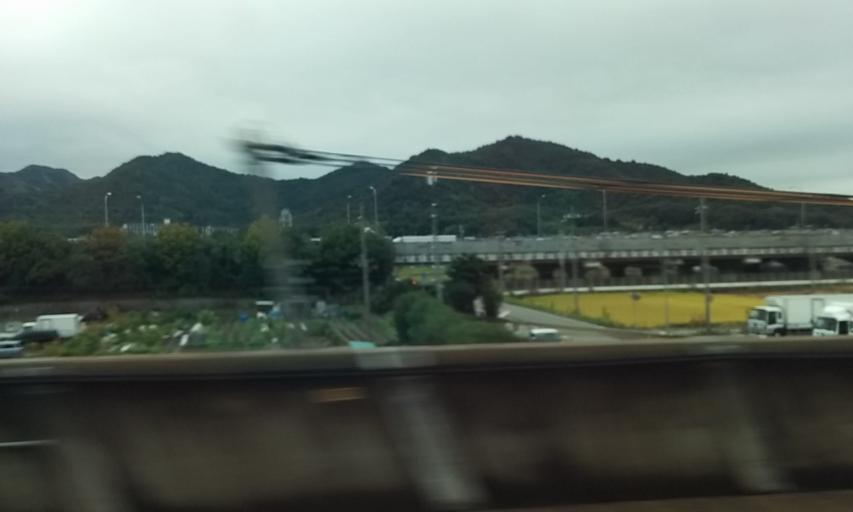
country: JP
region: Hyogo
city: Shirahamacho-usazakiminami
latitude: 34.7949
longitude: 134.7613
